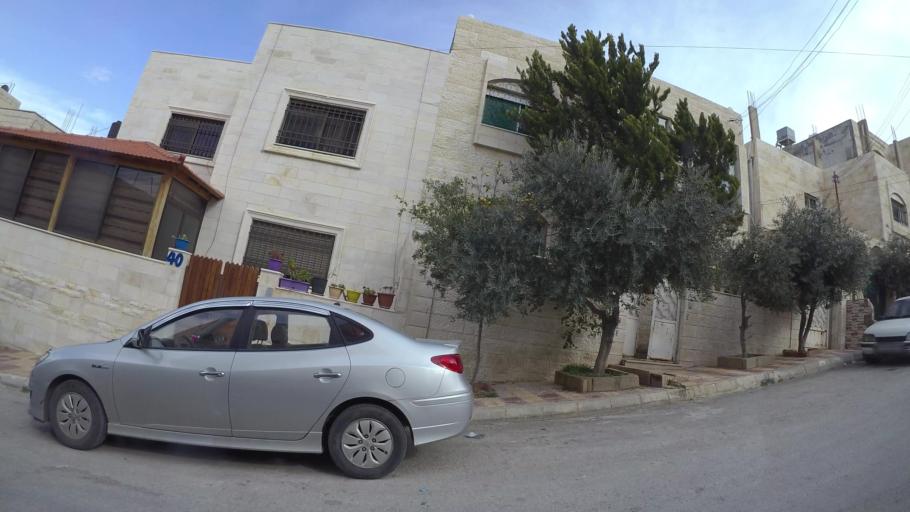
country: JO
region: Amman
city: Amman
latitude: 32.0141
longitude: 35.9443
